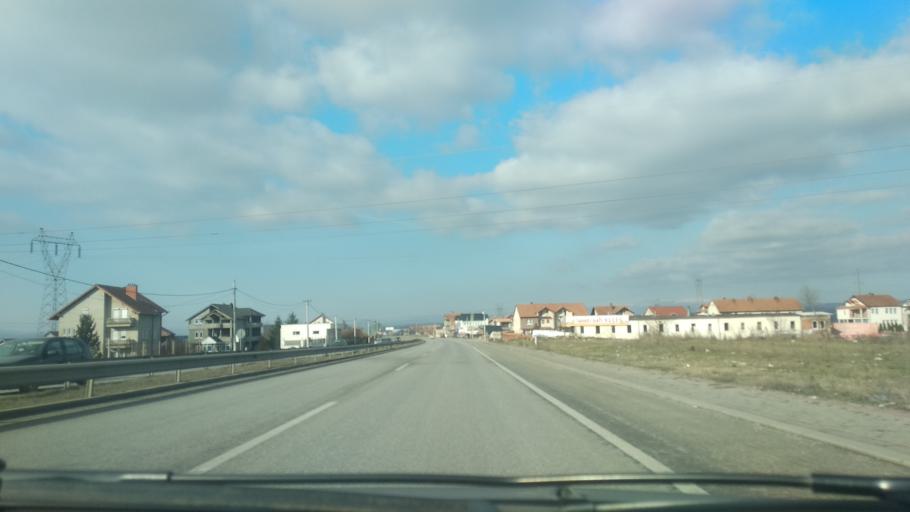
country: XK
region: Pristina
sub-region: Komuna e Obiliqit
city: Obiliq
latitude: 42.7049
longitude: 21.1073
